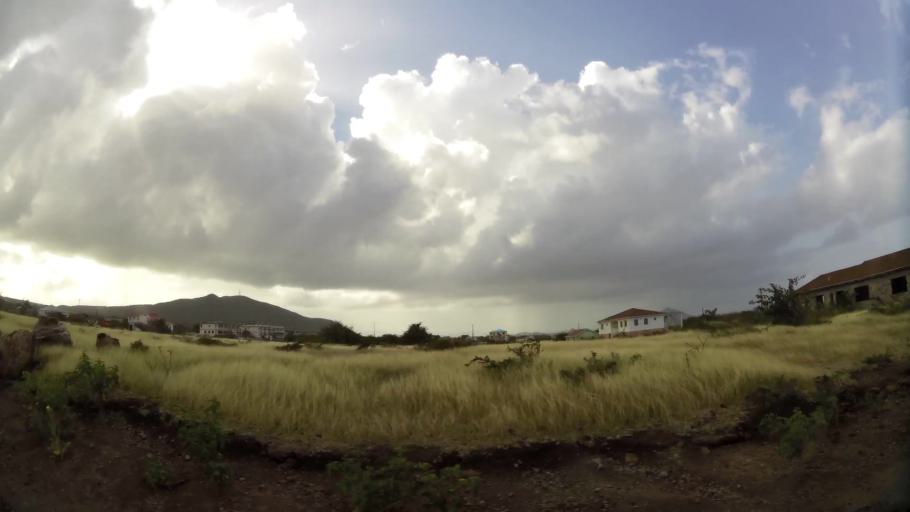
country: KN
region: Saint James Windwa
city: Newcastle
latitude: 17.1998
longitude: -62.5790
